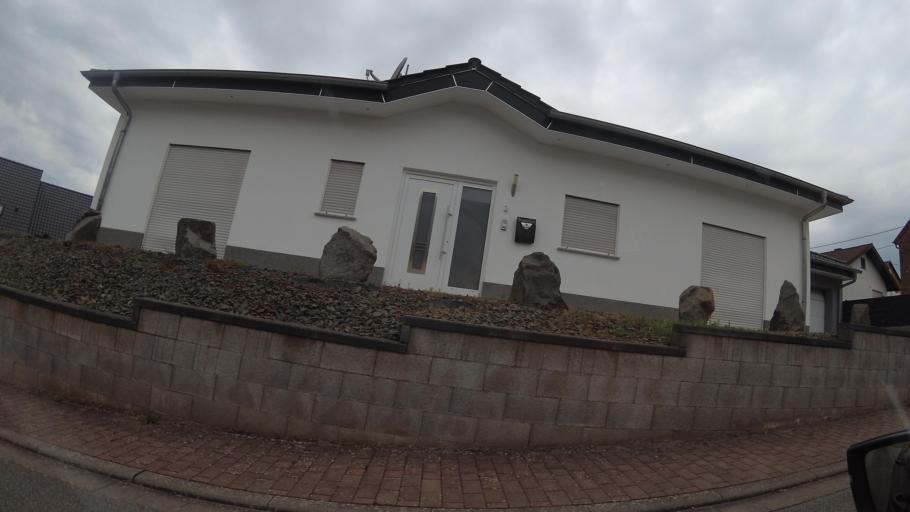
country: DE
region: Rheinland-Pfalz
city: Gries
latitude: 49.4189
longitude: 7.3961
